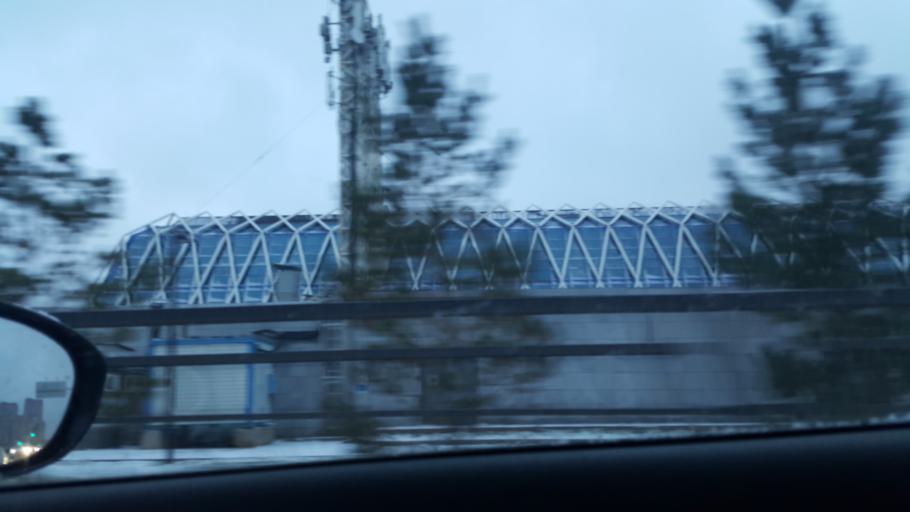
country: KZ
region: Astana Qalasy
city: Astana
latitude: 51.1201
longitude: 71.4738
